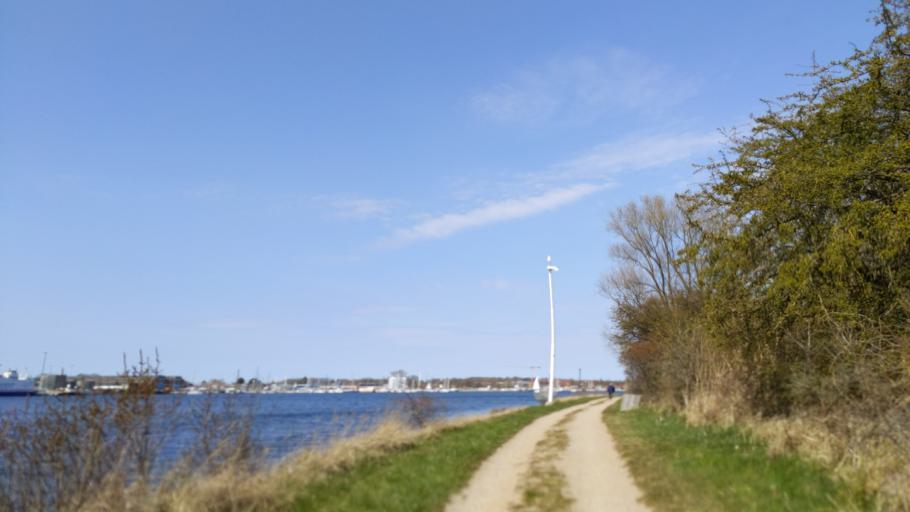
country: DE
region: Schleswig-Holstein
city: Travemuende
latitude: 53.9472
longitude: 10.8631
